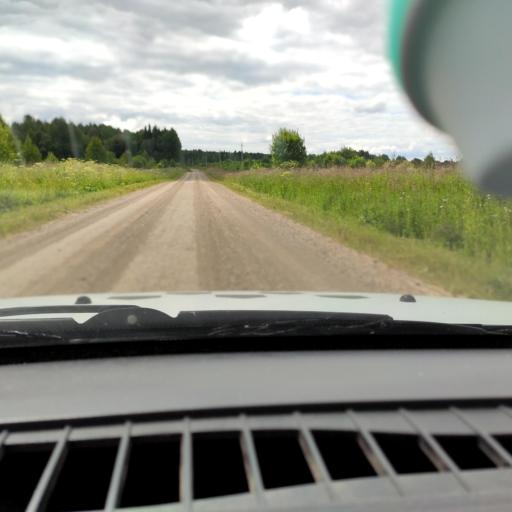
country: RU
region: Perm
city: Suksun
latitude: 57.2012
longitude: 57.6103
